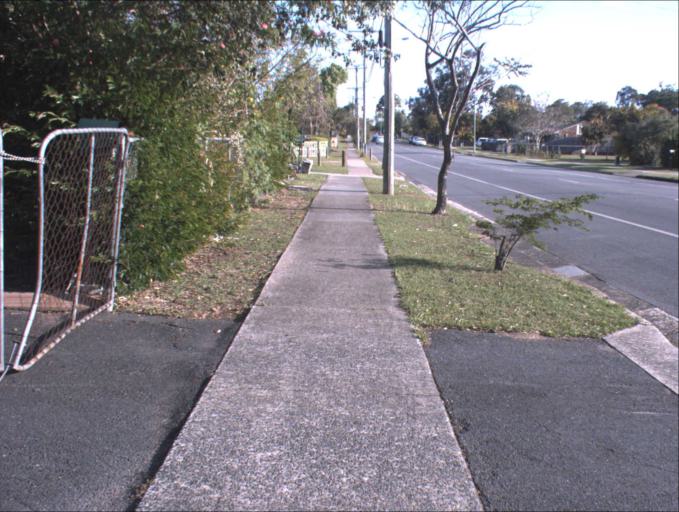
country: AU
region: Queensland
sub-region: Logan
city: Waterford West
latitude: -27.6787
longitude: 153.1005
